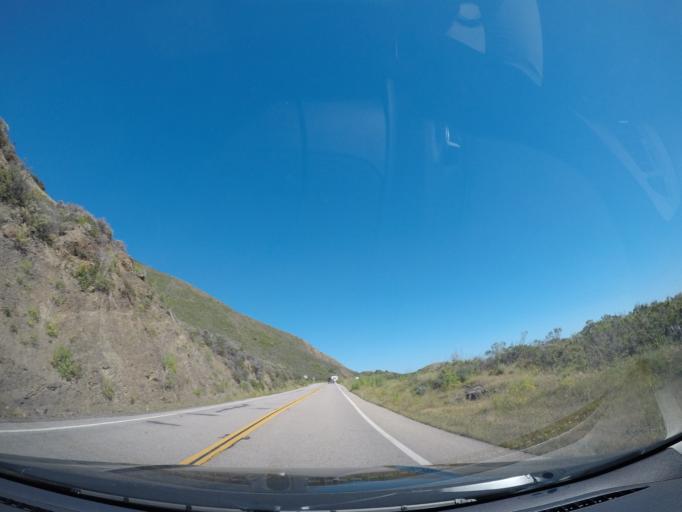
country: US
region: California
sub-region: San Luis Obispo County
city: Cambria
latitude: 35.8256
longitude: -121.3825
